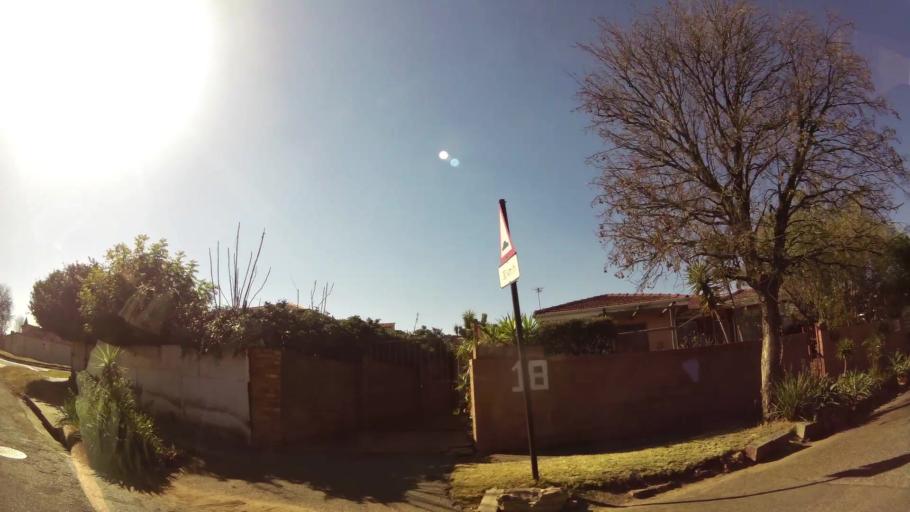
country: ZA
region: Gauteng
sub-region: City of Johannesburg Metropolitan Municipality
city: Johannesburg
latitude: -26.1908
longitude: 27.9837
